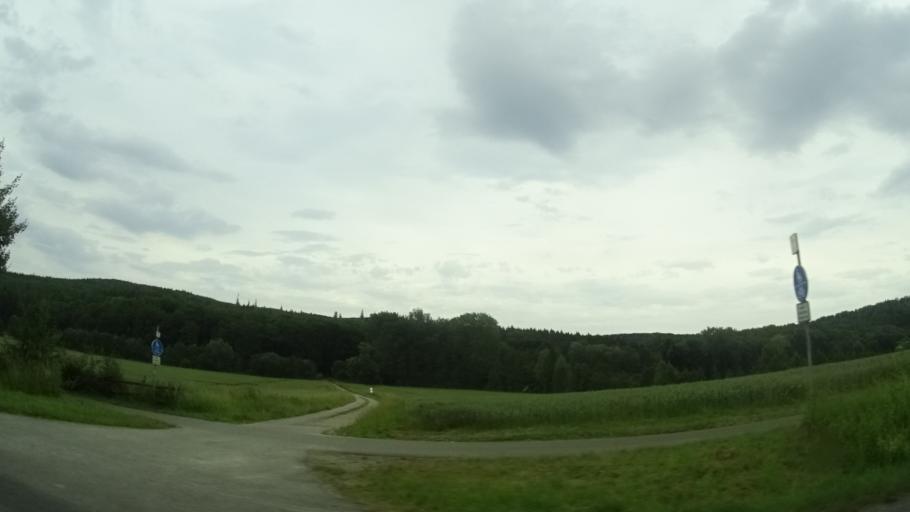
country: DE
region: North Rhine-Westphalia
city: Brakel
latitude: 51.7484
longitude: 9.1767
